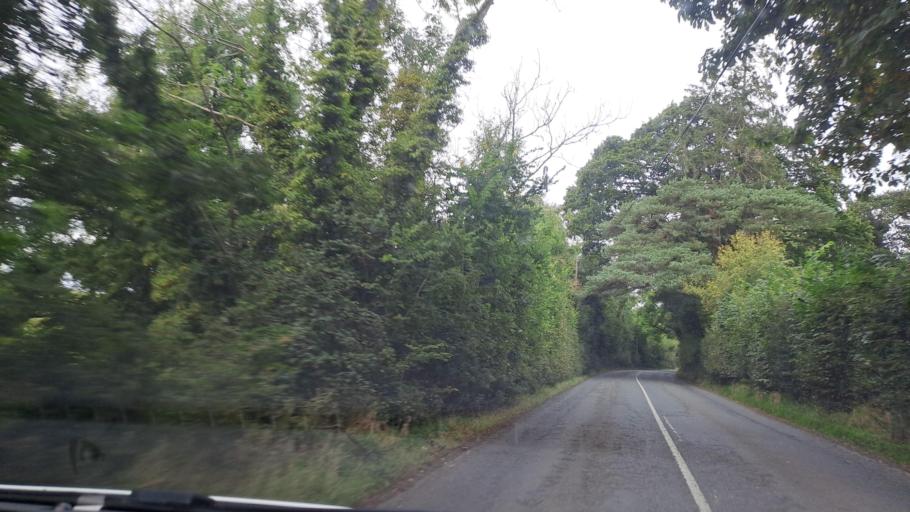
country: IE
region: Ulster
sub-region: County Monaghan
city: Carrickmacross
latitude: 53.8573
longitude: -6.6698
